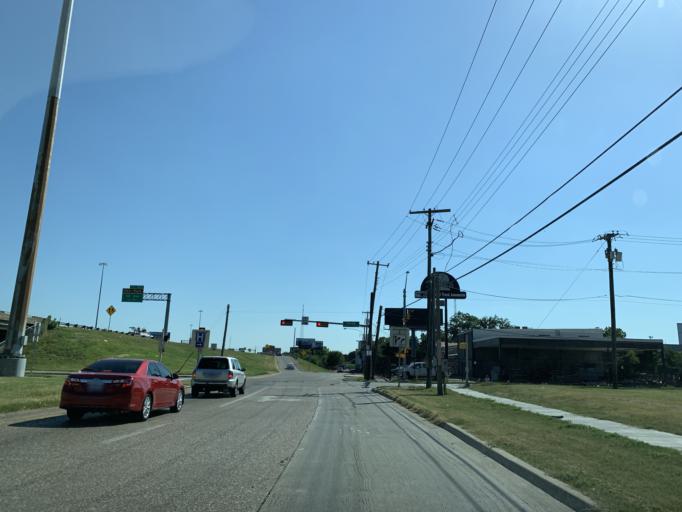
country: US
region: Texas
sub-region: Dallas County
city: Dallas
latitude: 32.7881
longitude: -96.7659
